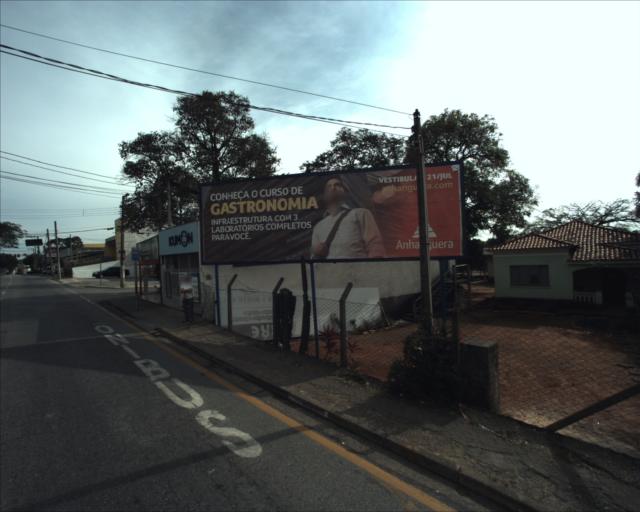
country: BR
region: Sao Paulo
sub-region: Sorocaba
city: Sorocaba
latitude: -23.4816
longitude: -47.4778
